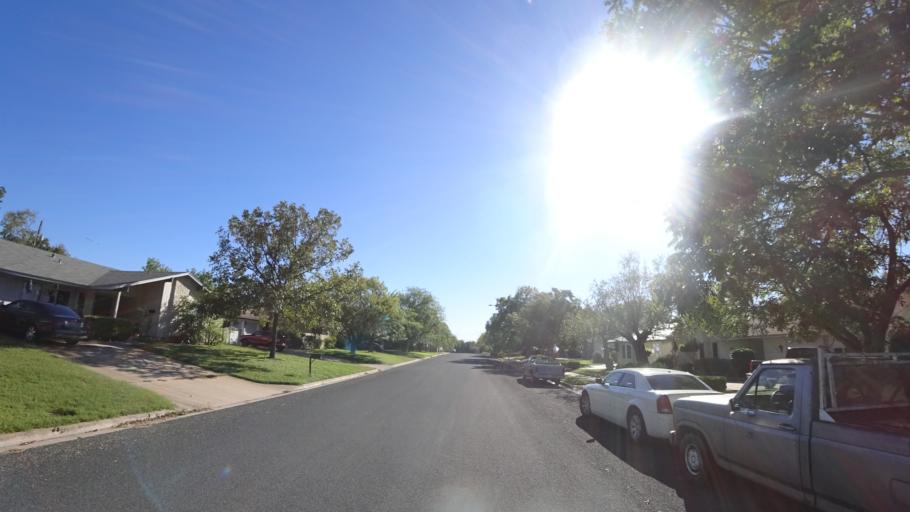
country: US
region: Texas
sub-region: Travis County
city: Austin
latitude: 30.2883
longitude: -97.6752
